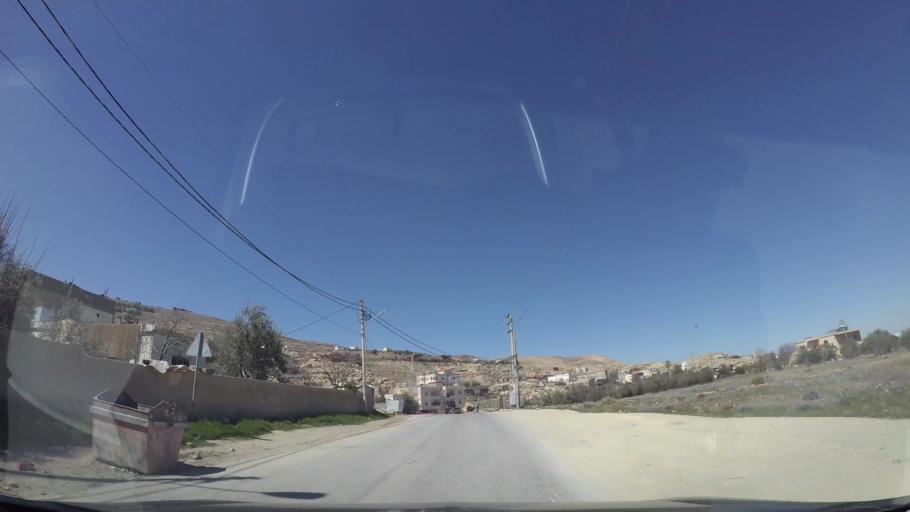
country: JO
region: Tafielah
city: At Tafilah
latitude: 30.8206
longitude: 35.5829
